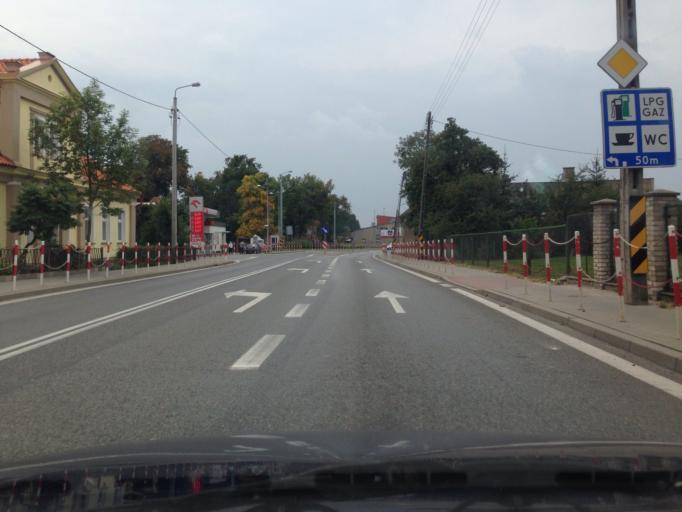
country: PL
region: Kujawsko-Pomorskie
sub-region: Powiat swiecki
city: Nowe
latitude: 53.6450
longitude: 18.7251
